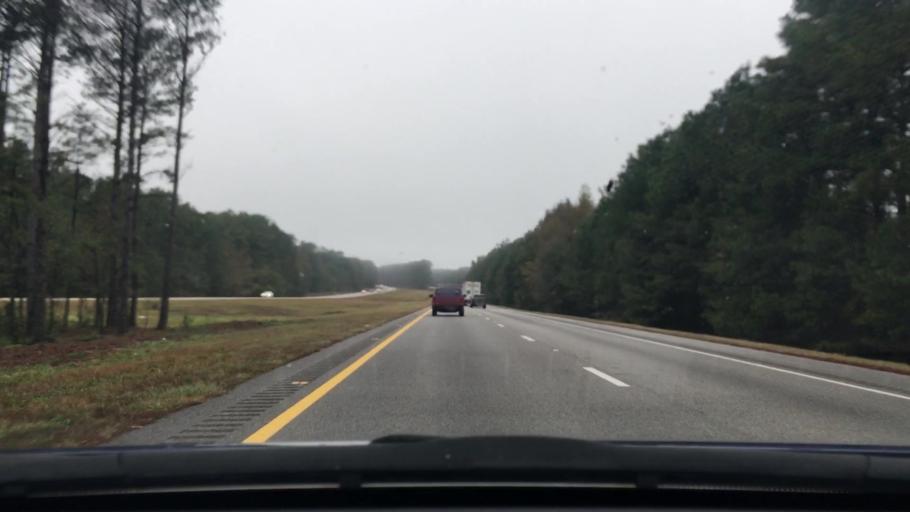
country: US
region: South Carolina
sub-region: Kershaw County
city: Camden
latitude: 34.2132
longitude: -80.4978
